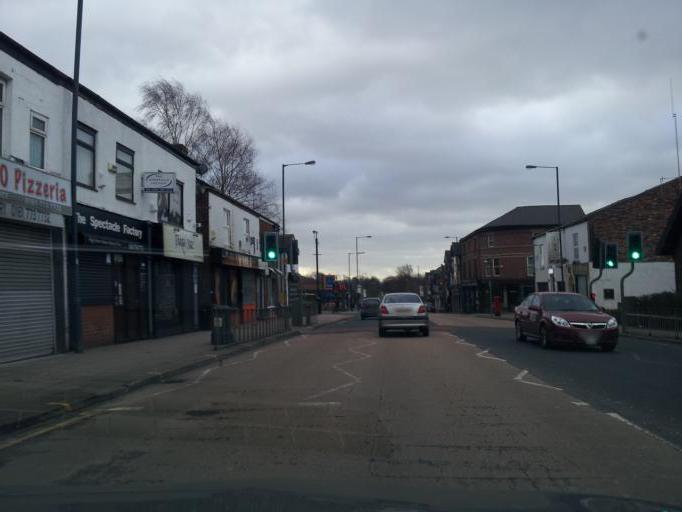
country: GB
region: England
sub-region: Borough of Bury
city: Prestwich
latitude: 53.5312
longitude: -2.2837
